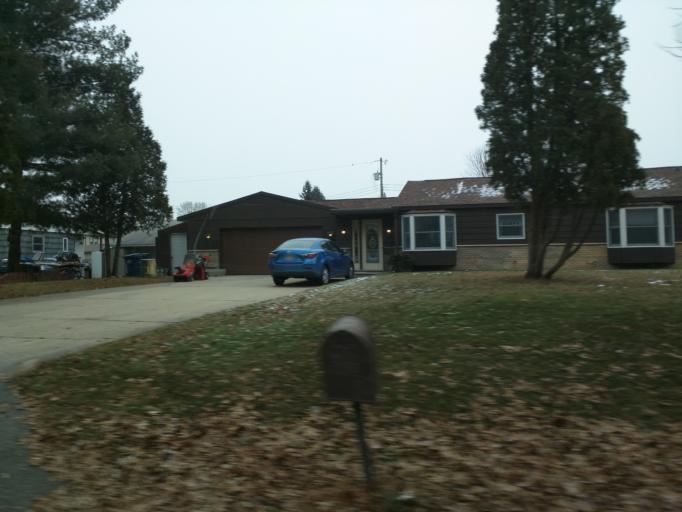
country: US
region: Wisconsin
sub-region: La Crosse County
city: French Island
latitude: 43.8536
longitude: -91.2684
